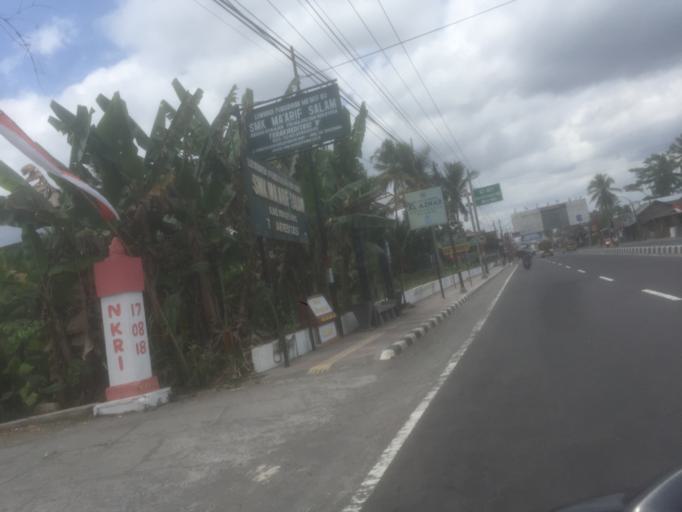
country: ID
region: Central Java
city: Muntilan
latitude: -7.6359
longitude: 110.3201
